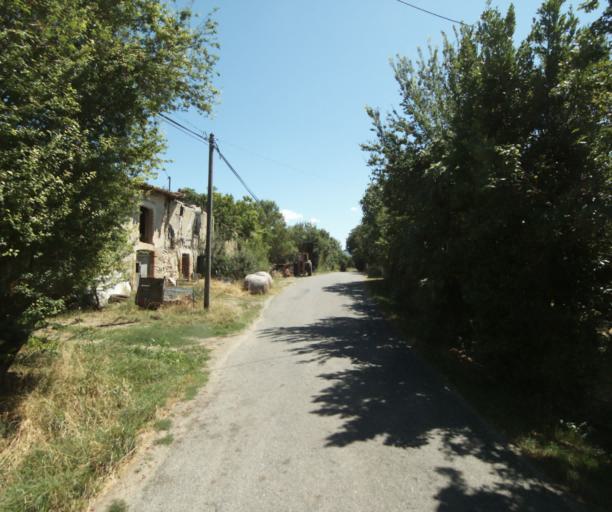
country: FR
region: Midi-Pyrenees
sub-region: Departement de la Haute-Garonne
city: Saint-Felix-Lauragais
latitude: 43.4623
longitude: 1.9365
